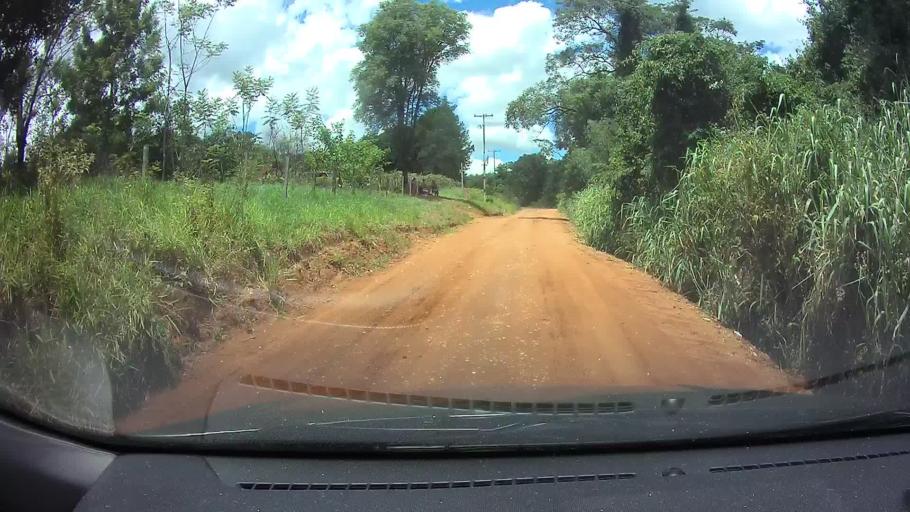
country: PY
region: Paraguari
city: La Colmena
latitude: -25.9238
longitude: -56.7933
